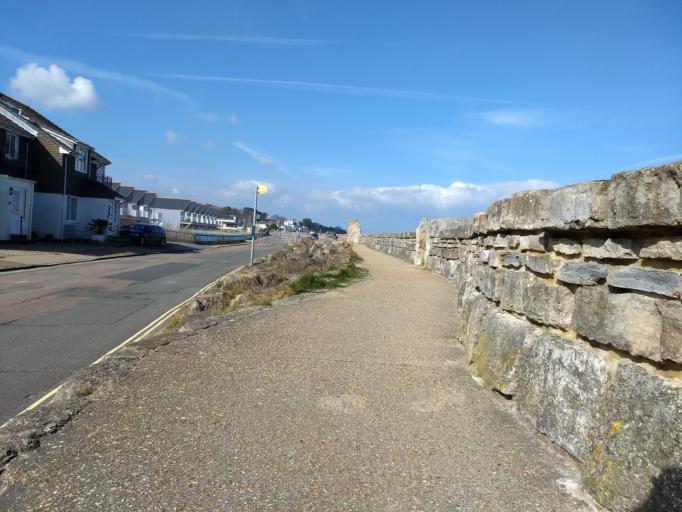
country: GB
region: England
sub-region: Isle of Wight
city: Seaview
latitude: 50.7223
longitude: -1.1162
